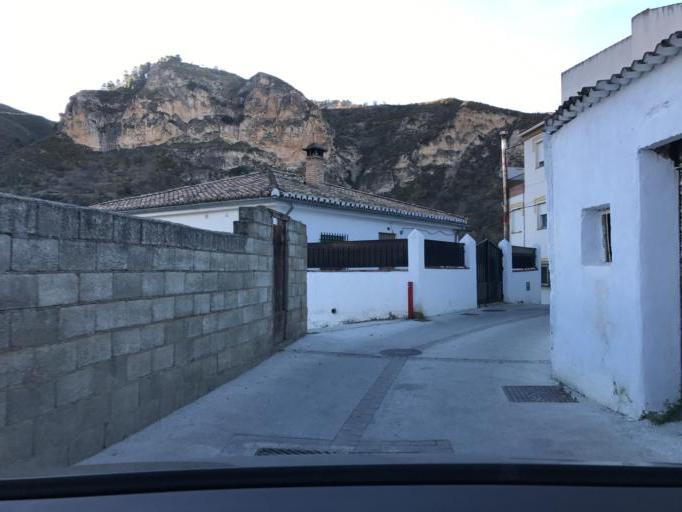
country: ES
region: Andalusia
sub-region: Provincia de Granada
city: Quentar
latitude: 37.1927
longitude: -3.4643
